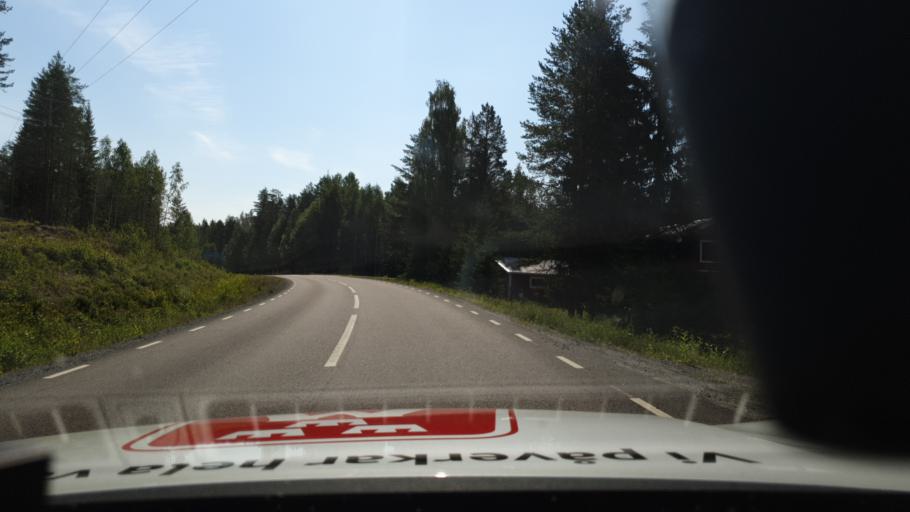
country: SE
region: Norrbotten
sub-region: Lulea Kommun
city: Sodra Sunderbyn
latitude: 65.8209
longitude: 21.8942
